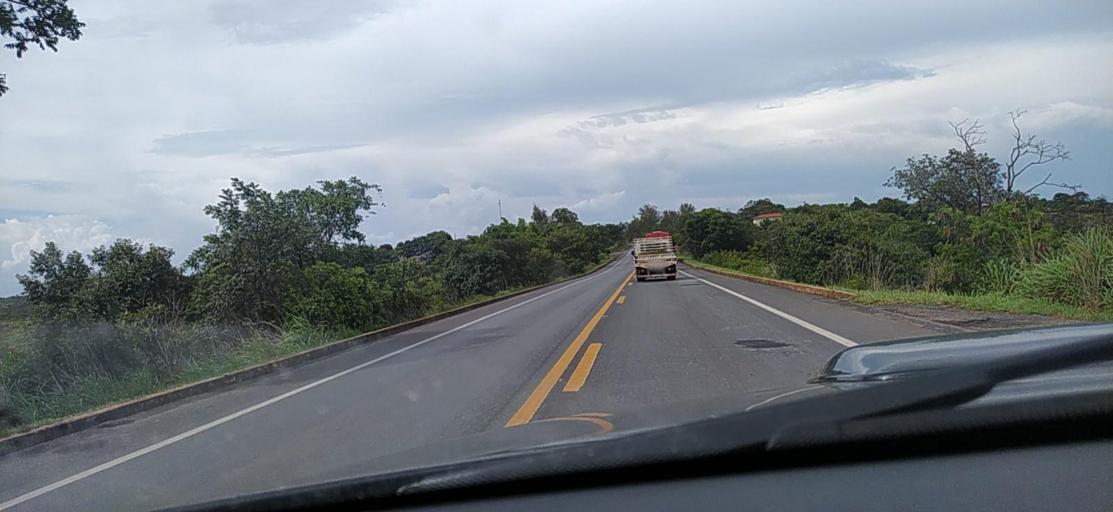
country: BR
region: Minas Gerais
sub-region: Montes Claros
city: Montes Claros
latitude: -16.8430
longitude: -43.8502
